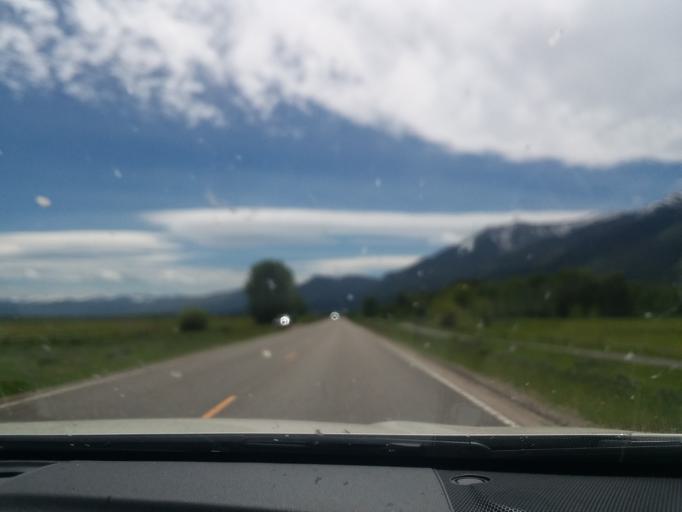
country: US
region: Wyoming
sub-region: Teton County
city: Moose Wilson Road
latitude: 43.5911
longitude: -110.8138
